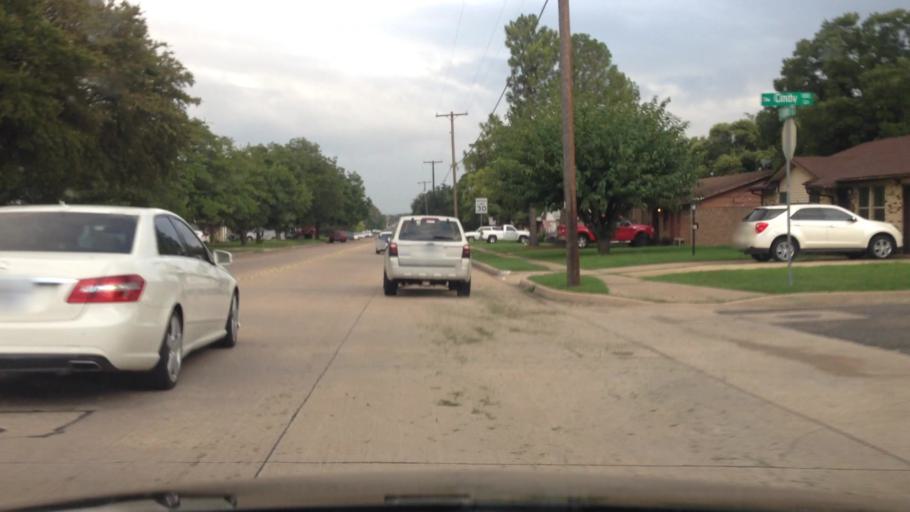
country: US
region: Texas
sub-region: Johnson County
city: Burleson
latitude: 32.5506
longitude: -97.3339
